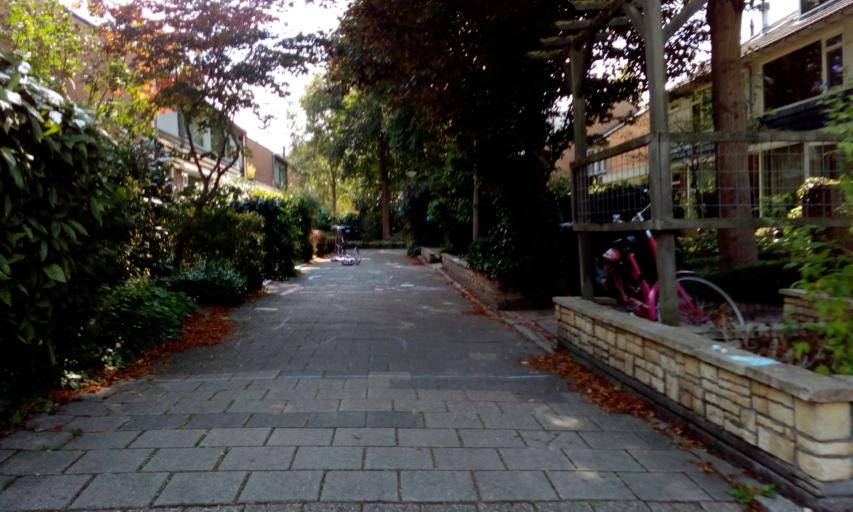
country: NL
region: South Holland
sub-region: Gemeente Gouda
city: Bloemendaal
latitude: 52.0284
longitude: 4.6883
